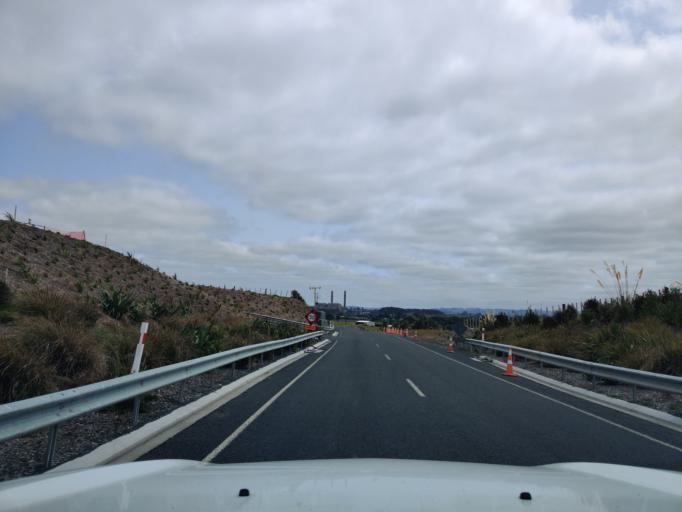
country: NZ
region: Waikato
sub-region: Waikato District
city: Te Kauwhata
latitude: -37.5234
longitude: 175.1749
